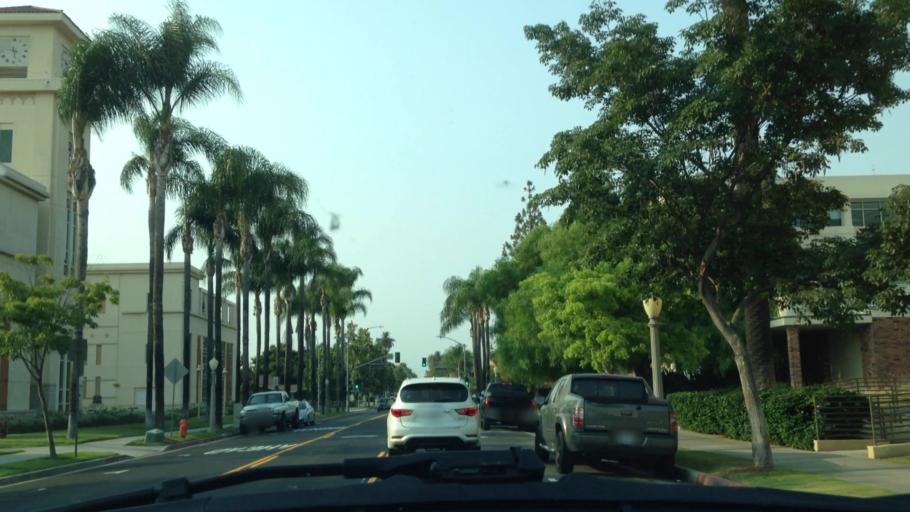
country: US
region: California
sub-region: Orange County
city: Orange
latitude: 33.7921
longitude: -117.8531
